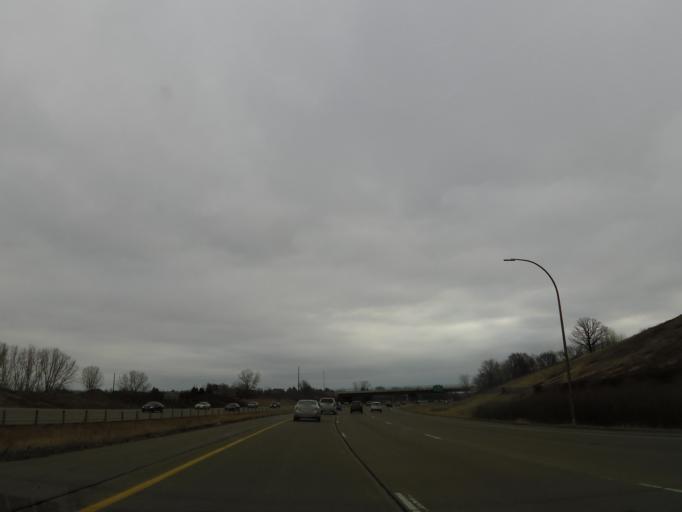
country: US
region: Minnesota
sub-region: Dakota County
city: Eagan
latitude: 44.8088
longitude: -93.1867
